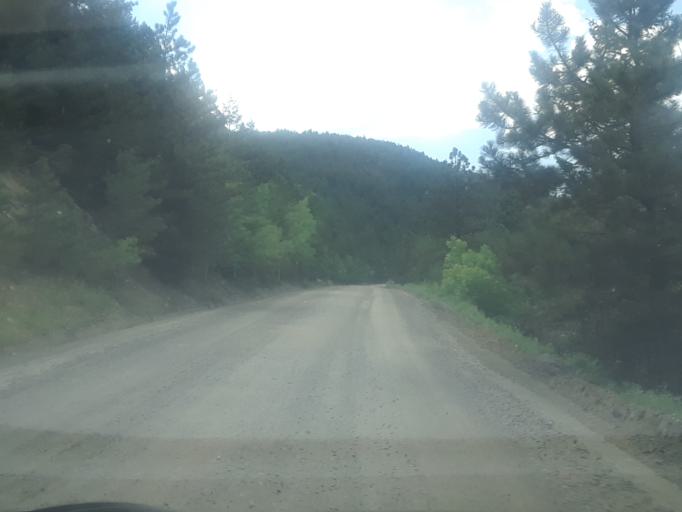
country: US
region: Colorado
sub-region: Boulder County
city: Boulder
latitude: 40.0687
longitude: -105.3801
